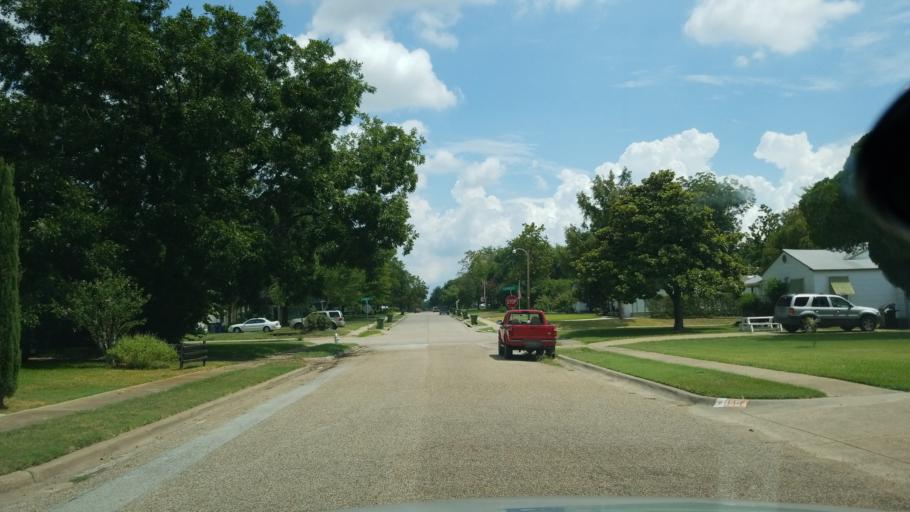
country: US
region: Texas
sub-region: Dallas County
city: Garland
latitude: 32.9180
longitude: -96.6526
